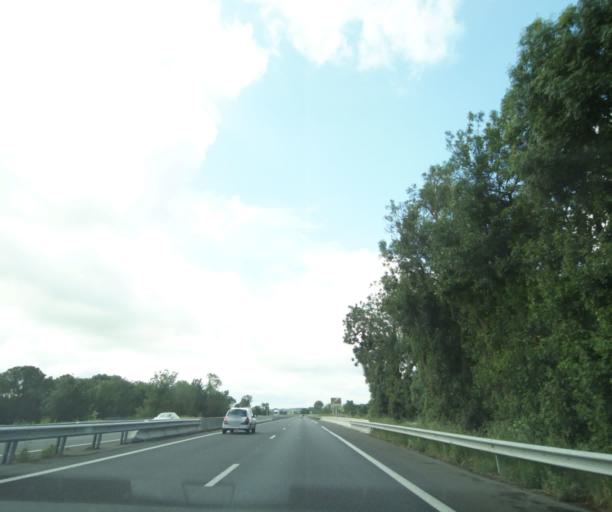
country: FR
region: Pays de la Loire
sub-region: Departement de Maine-et-Loire
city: Vivy
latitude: 47.2941
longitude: -0.0415
